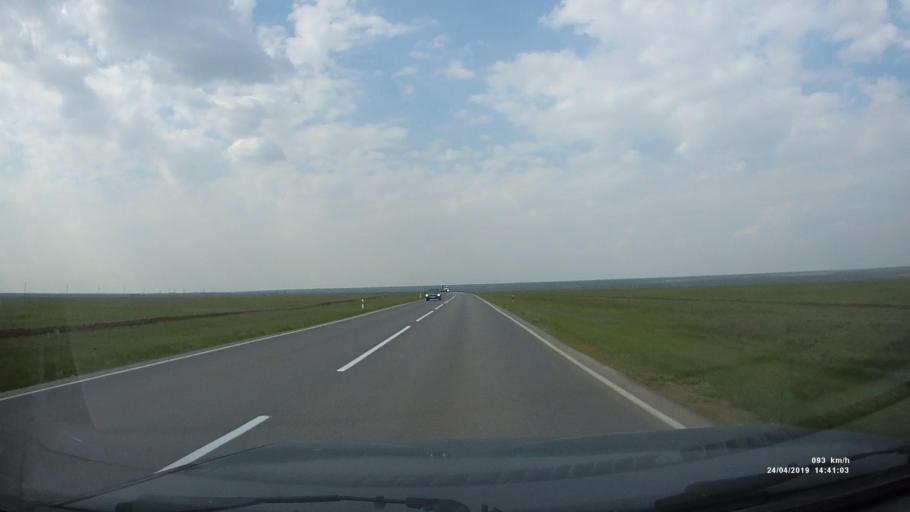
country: RU
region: Rostov
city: Remontnoye
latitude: 46.4407
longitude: 43.8838
